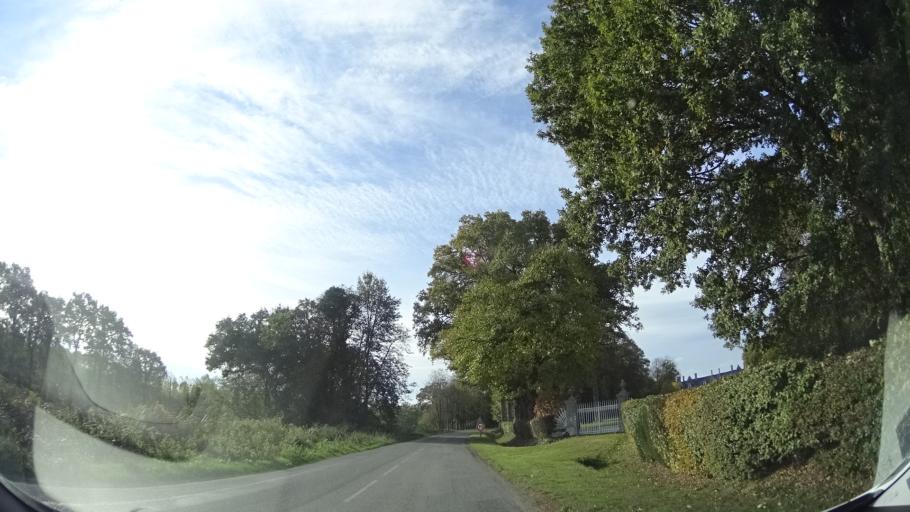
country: FR
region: Brittany
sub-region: Departement d'Ille-et-Vilaine
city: Romille
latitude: 48.2138
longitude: -1.9172
